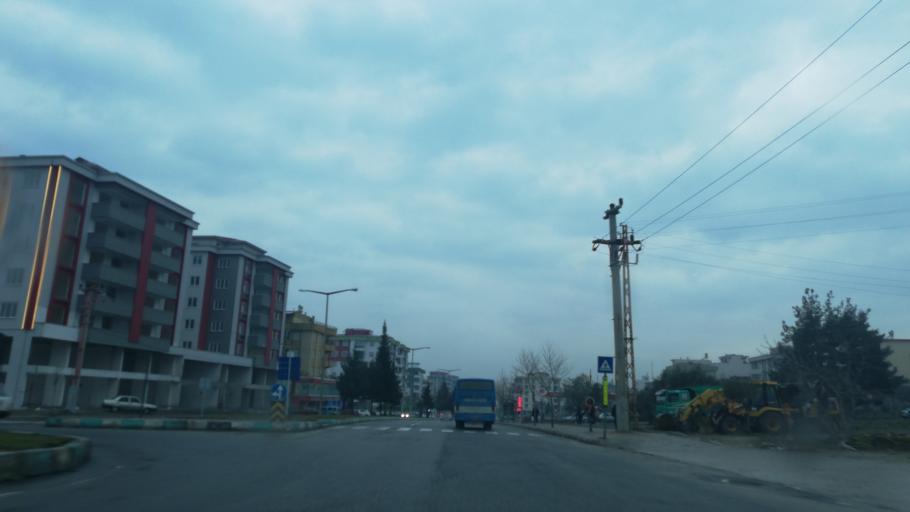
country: TR
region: Kahramanmaras
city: Kahramanmaras
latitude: 37.5823
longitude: 36.9744
